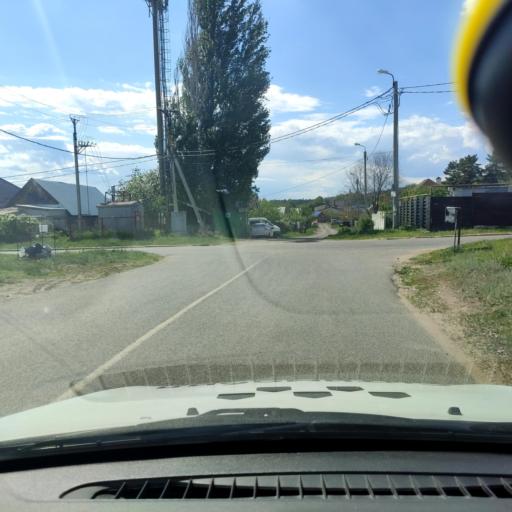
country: RU
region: Samara
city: Zhigulevsk
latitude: 53.4692
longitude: 49.6322
